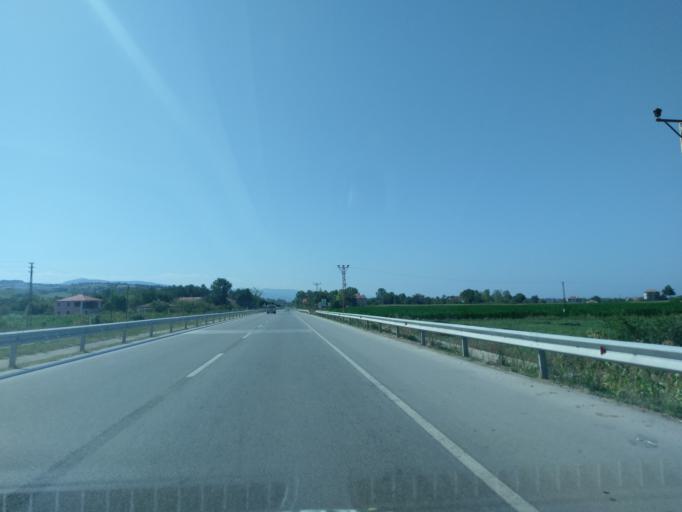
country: TR
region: Samsun
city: Alacam
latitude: 41.6097
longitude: 35.6558
